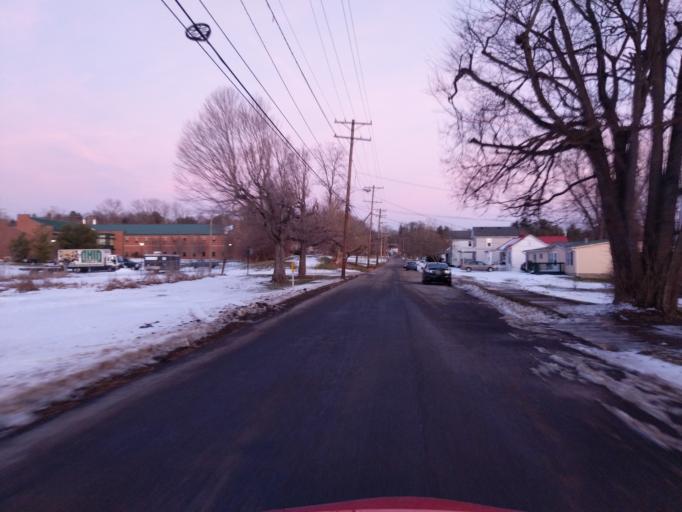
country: US
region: Ohio
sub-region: Athens County
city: Athens
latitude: 39.3338
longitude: -82.1173
